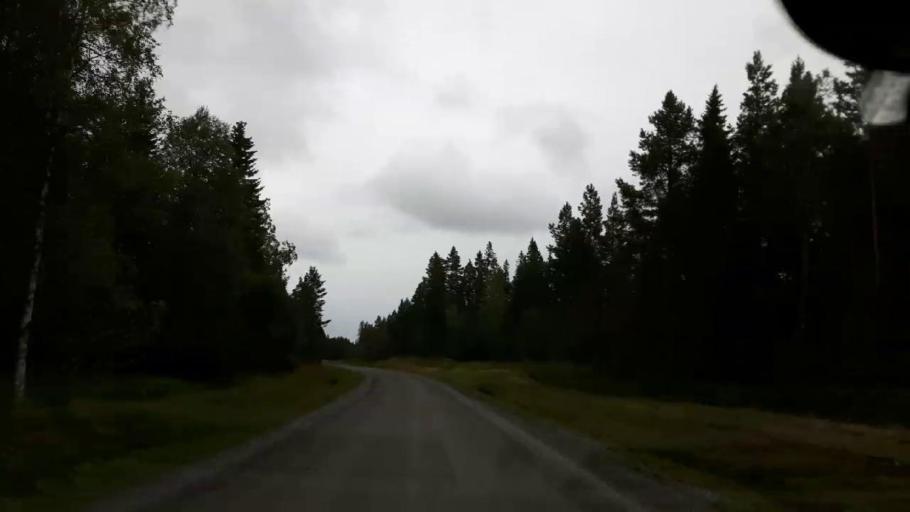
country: SE
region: Jaemtland
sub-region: OEstersunds Kommun
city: Ostersund
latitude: 63.0792
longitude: 14.5551
